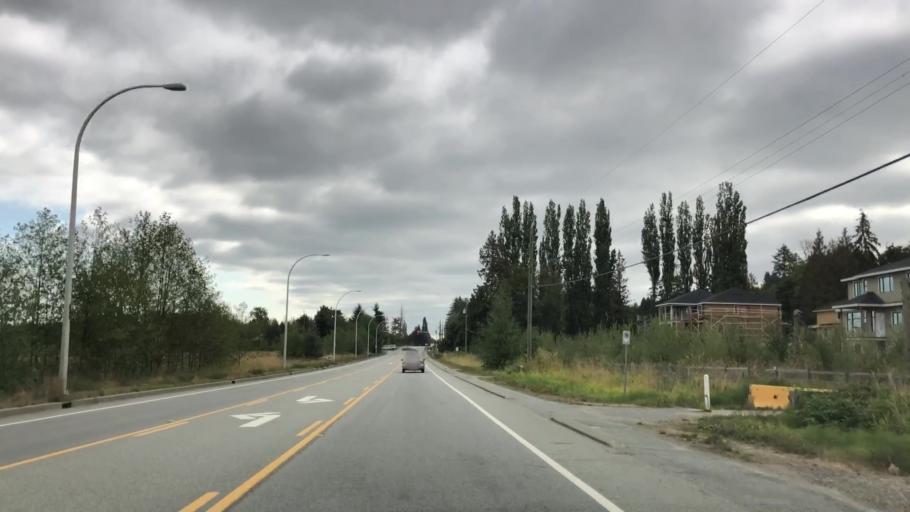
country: CA
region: British Columbia
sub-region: Greater Vancouver Regional District
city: White Rock
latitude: 49.0603
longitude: -122.7611
